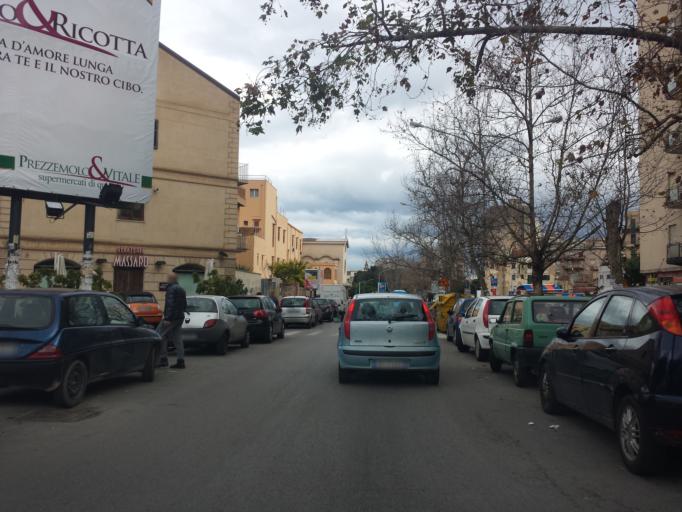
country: IT
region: Sicily
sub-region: Palermo
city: Palermo
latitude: 38.1071
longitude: 13.3538
